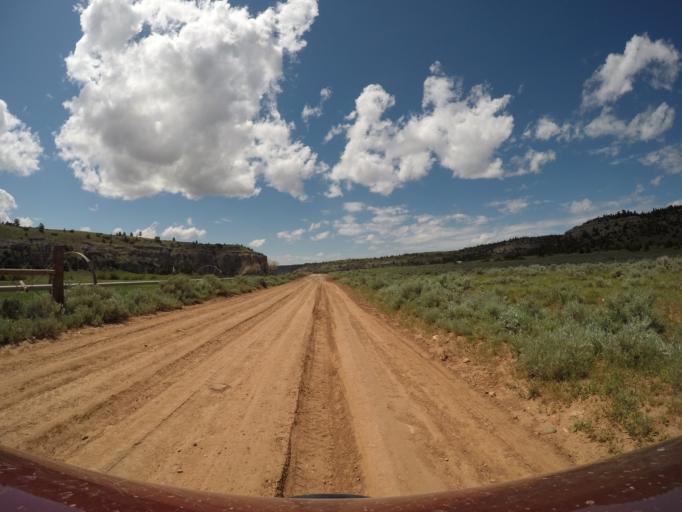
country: US
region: Montana
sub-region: Yellowstone County
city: Laurel
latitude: 45.2404
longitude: -108.6355
